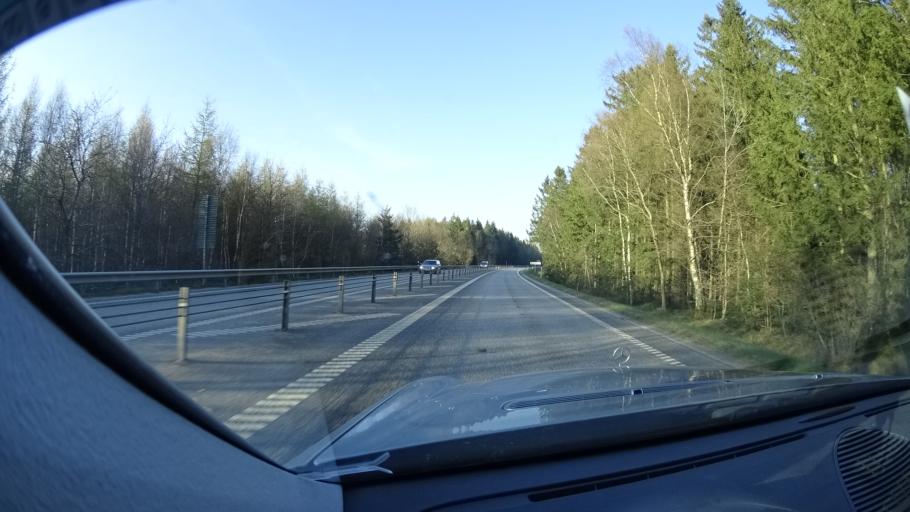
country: SE
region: Skane
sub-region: Hoors Kommun
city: Hoeoer
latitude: 55.9139
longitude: 13.5260
